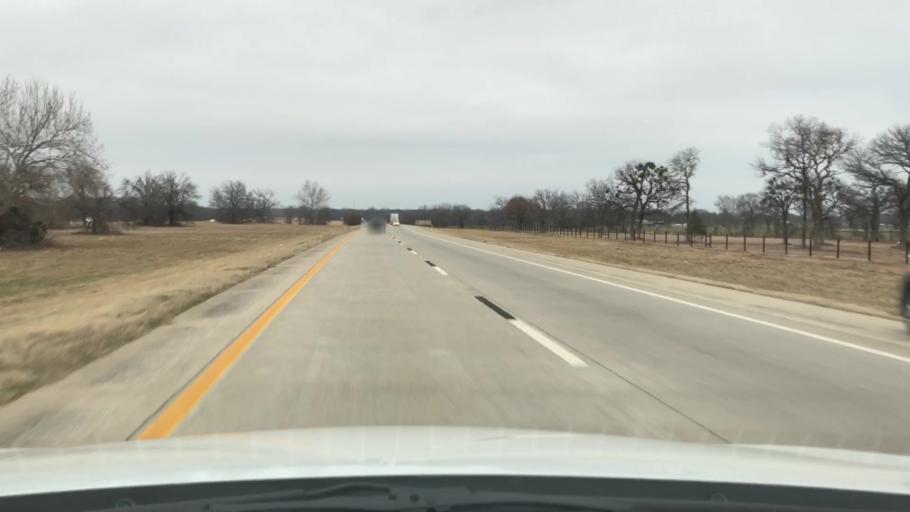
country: US
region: Oklahoma
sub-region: Love County
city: Marietta
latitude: 33.8143
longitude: -97.1325
